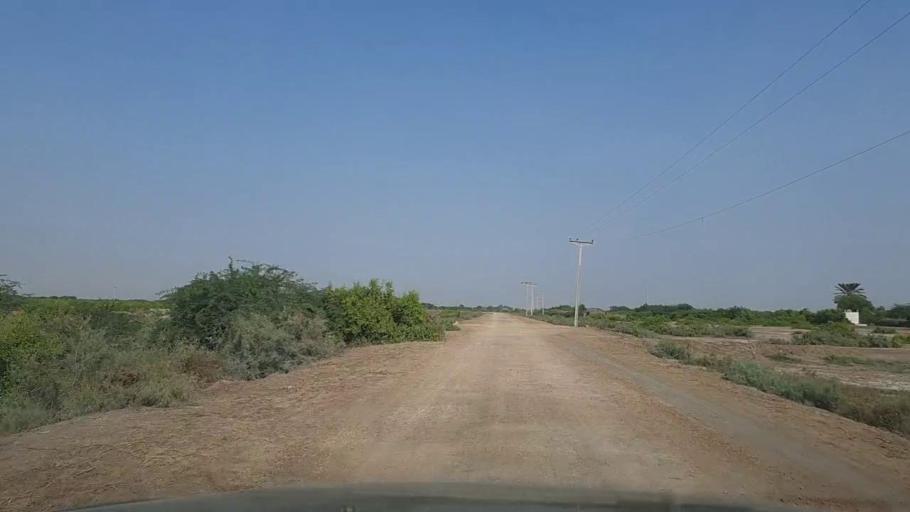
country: PK
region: Sindh
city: Thatta
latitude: 24.6050
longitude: 67.9542
